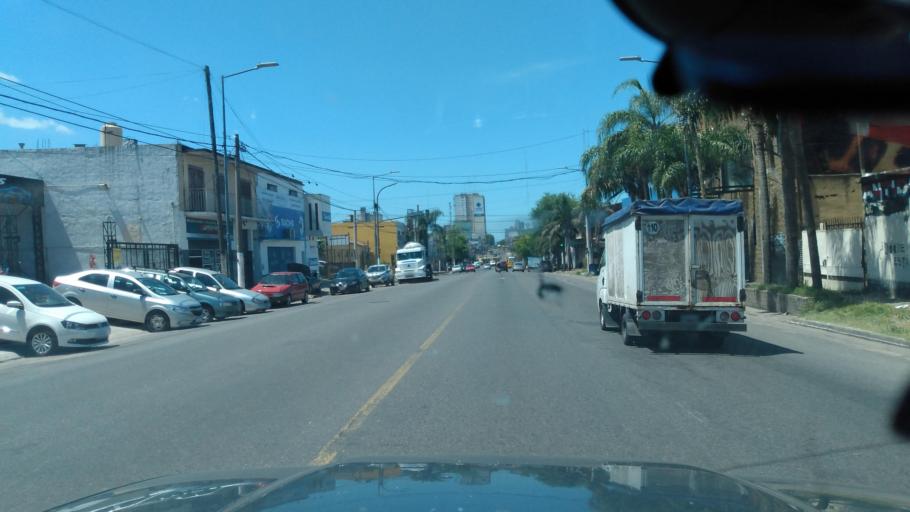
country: AR
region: Buenos Aires
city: Hurlingham
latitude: -34.5487
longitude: -58.7189
